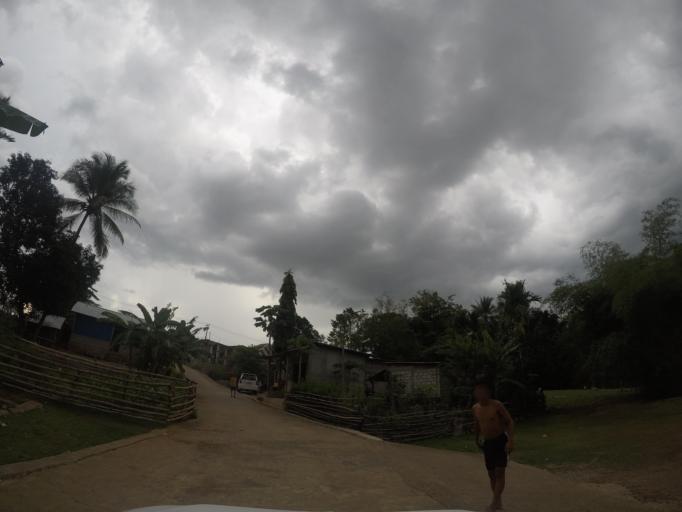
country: TL
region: Bobonaro
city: Maliana
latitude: -8.9745
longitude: 125.2202
